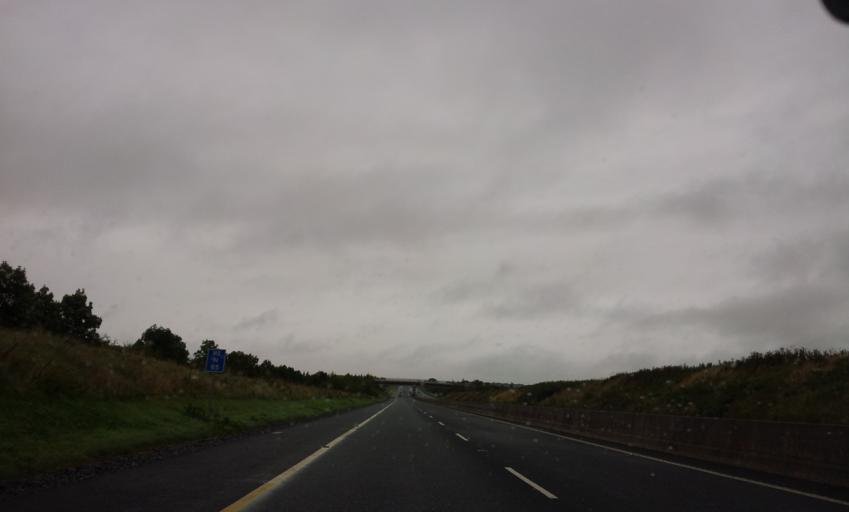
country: IE
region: Munster
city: Cashel
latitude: 52.4528
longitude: -7.9085
